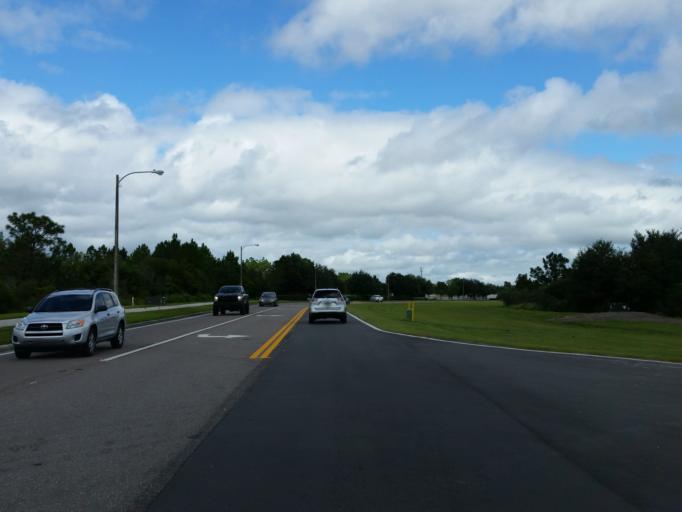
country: US
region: Florida
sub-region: Pasco County
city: Wesley Chapel
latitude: 28.2035
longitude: -82.2998
